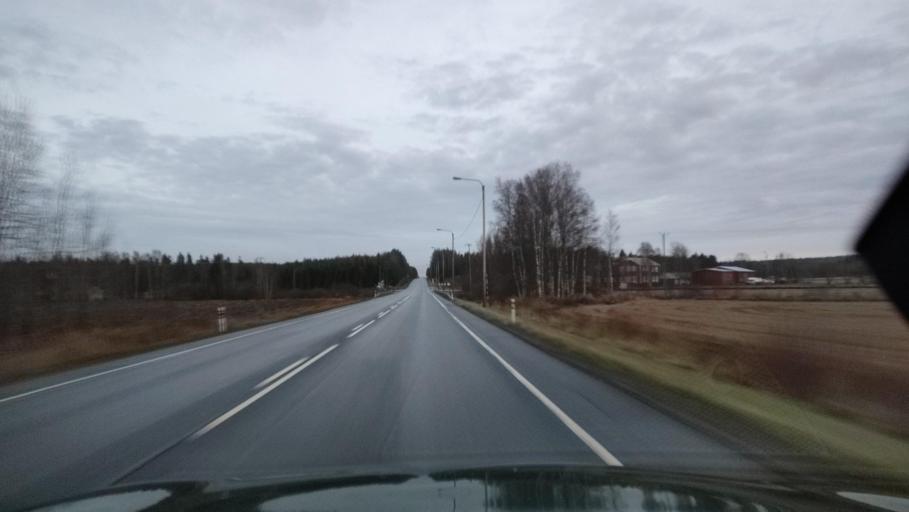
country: FI
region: Ostrobothnia
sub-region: Vaasa
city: Ristinummi
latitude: 62.9726
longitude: 21.7682
